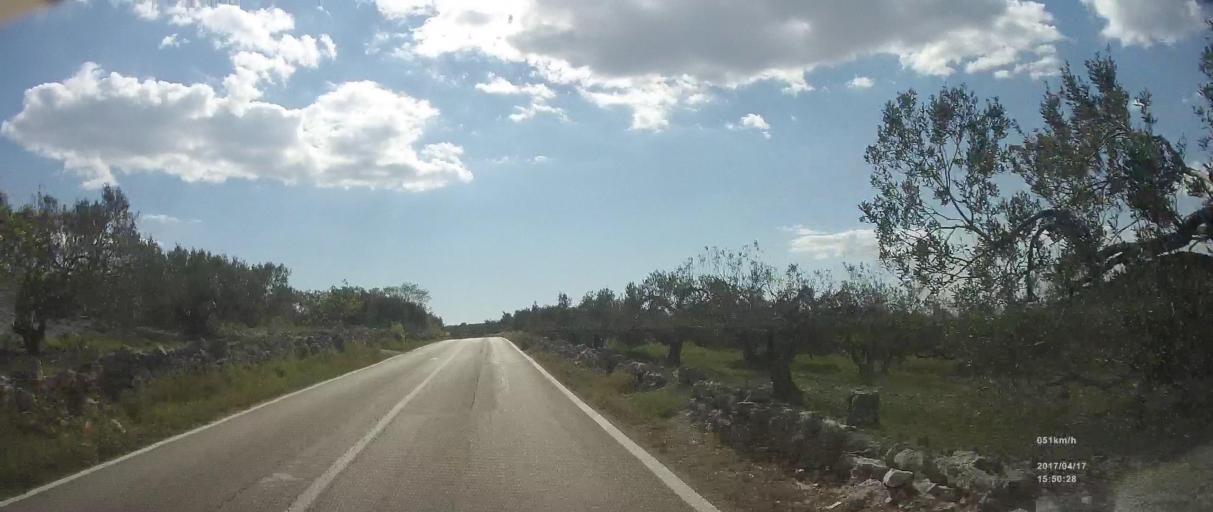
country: HR
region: Sibensko-Kniniska
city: Primosten
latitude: 43.6080
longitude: 15.9721
